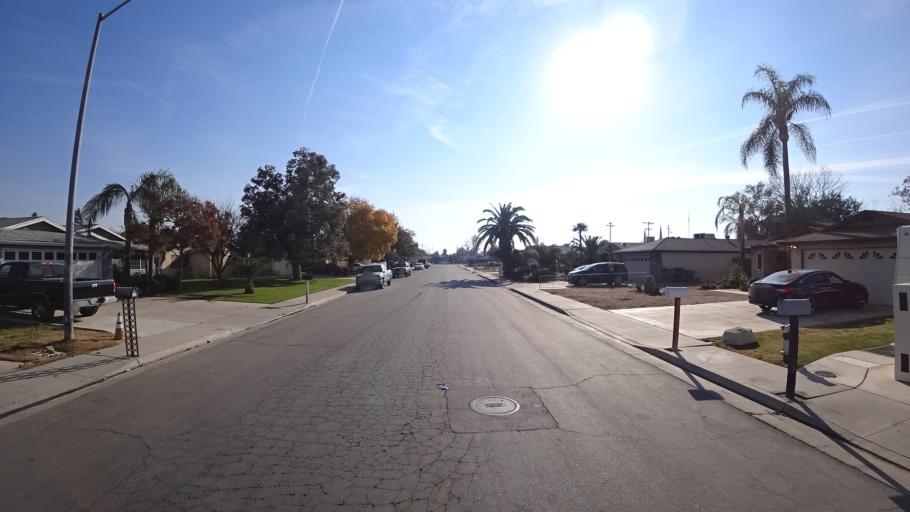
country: US
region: California
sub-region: Kern County
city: Greenfield
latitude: 35.3190
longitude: -119.0089
